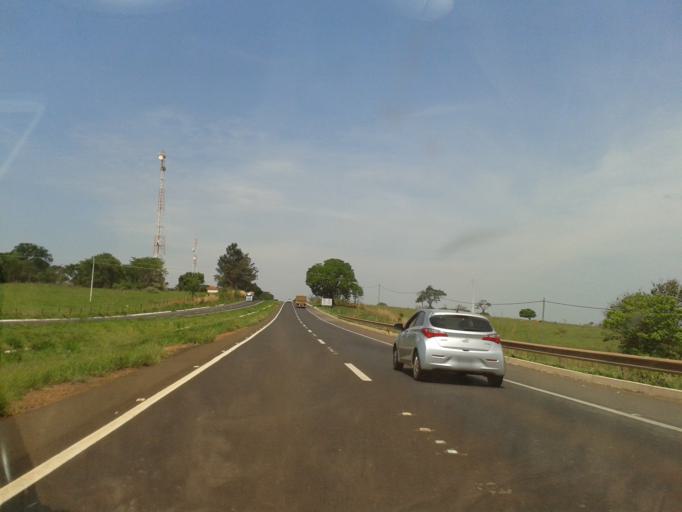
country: BR
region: Minas Gerais
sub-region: Monte Alegre De Minas
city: Monte Alegre de Minas
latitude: -18.8905
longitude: -48.6976
